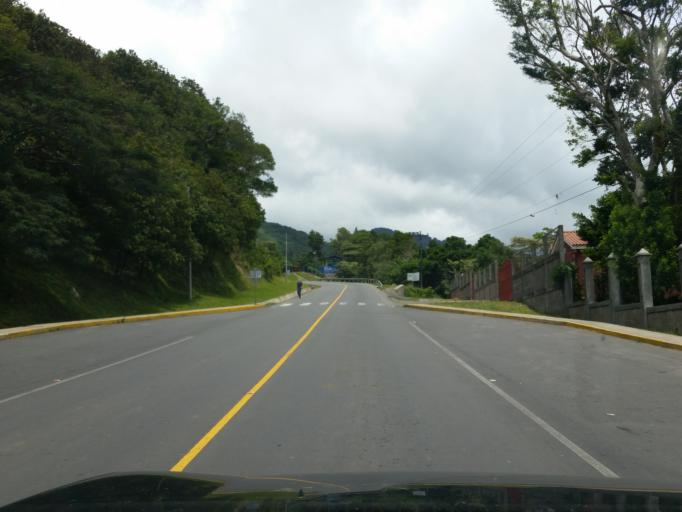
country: NI
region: Matagalpa
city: Matagalpa
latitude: 12.9733
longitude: -85.9206
